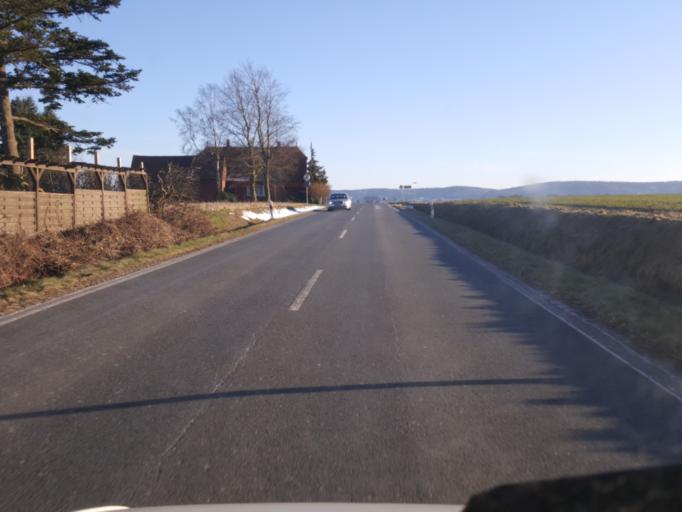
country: DE
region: North Rhine-Westphalia
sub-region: Regierungsbezirk Detmold
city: Hille
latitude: 52.3510
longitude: 8.7320
